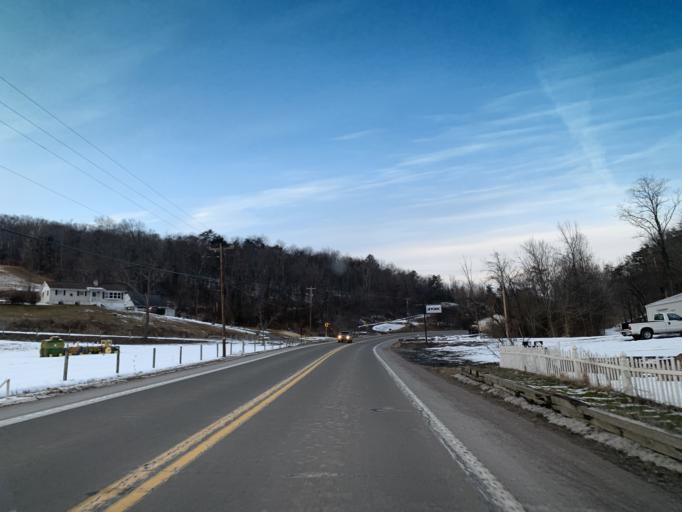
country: US
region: Maryland
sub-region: Allegany County
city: Cumberland
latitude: 39.7294
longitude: -78.7121
